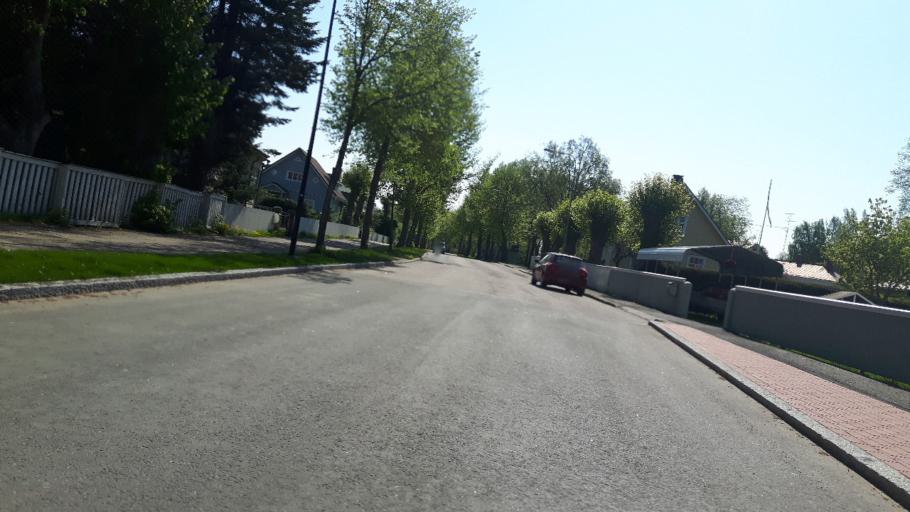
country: FI
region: Uusimaa
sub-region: Loviisa
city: Lovisa
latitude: 60.4472
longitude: 26.2364
